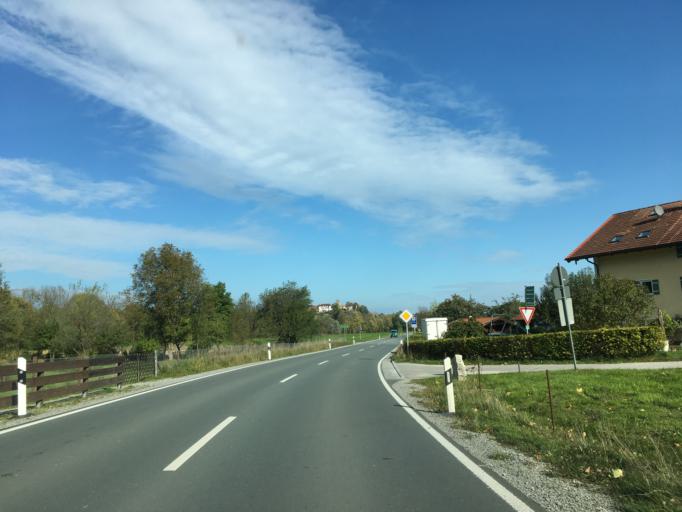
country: DE
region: Bavaria
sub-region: Upper Bavaria
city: Altenmarkt
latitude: 47.7605
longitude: 12.1374
